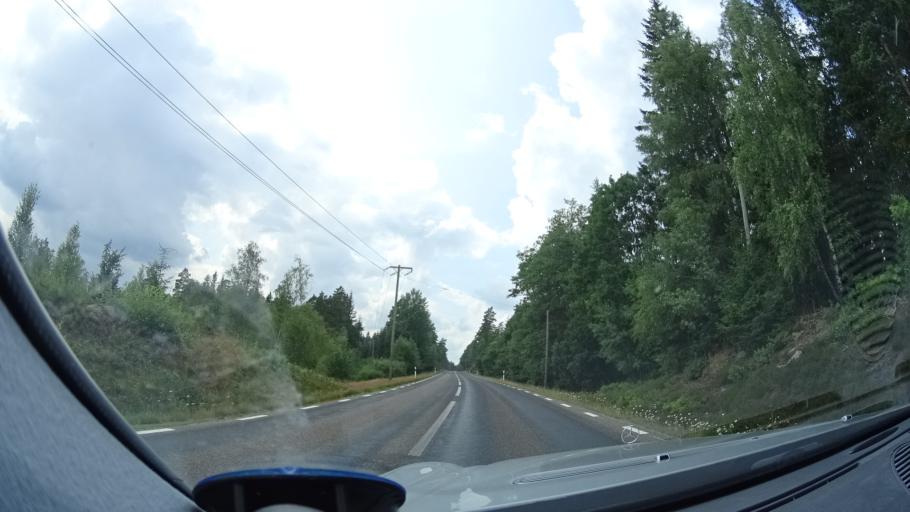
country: SE
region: Kalmar
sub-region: Emmaboda Kommun
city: Emmaboda
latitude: 56.6293
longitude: 15.6245
